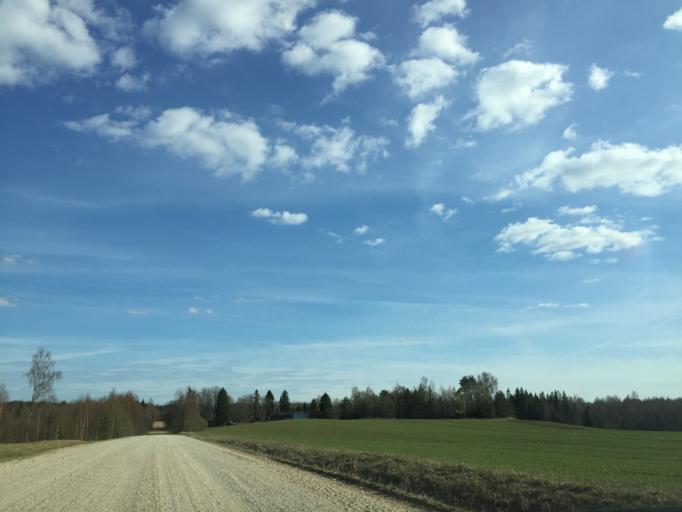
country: EE
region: Tartu
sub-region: Elva linn
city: Elva
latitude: 58.1198
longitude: 26.5294
